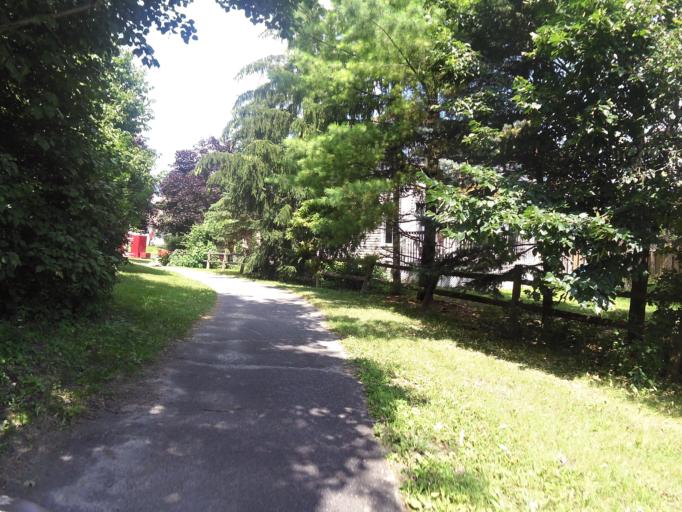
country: CA
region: Ontario
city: Bells Corners
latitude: 45.3138
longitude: -75.9192
